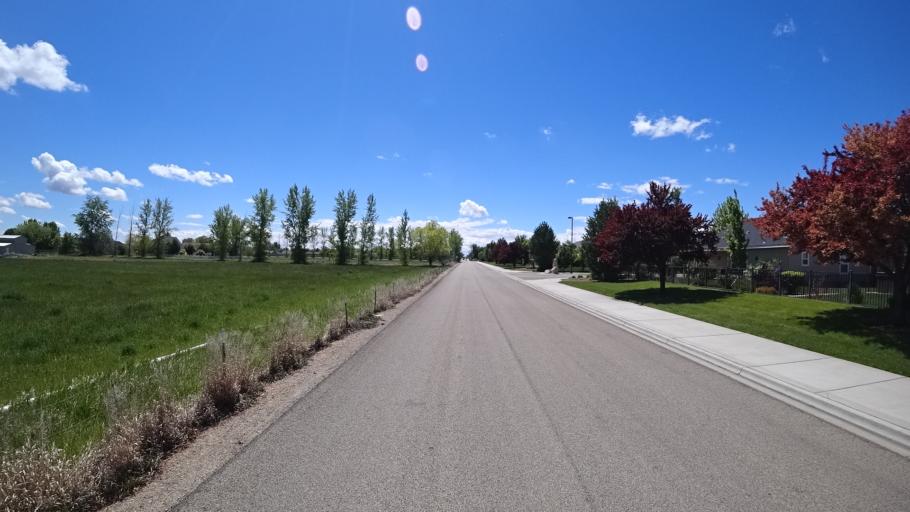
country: US
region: Idaho
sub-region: Ada County
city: Kuna
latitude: 43.5051
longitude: -116.4238
